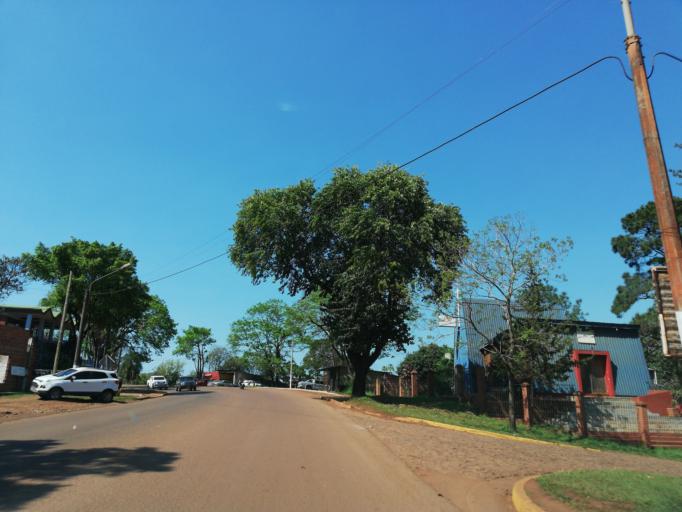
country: AR
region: Misiones
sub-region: Departamento de Eldorado
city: Eldorado
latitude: -26.4082
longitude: -54.6467
